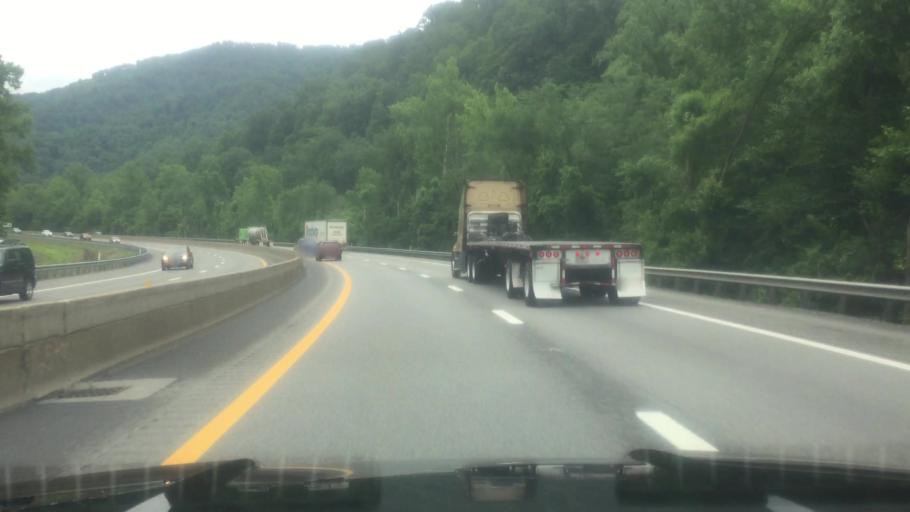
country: US
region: West Virginia
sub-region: Kanawha County
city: Montgomery
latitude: 38.0727
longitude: -81.3797
